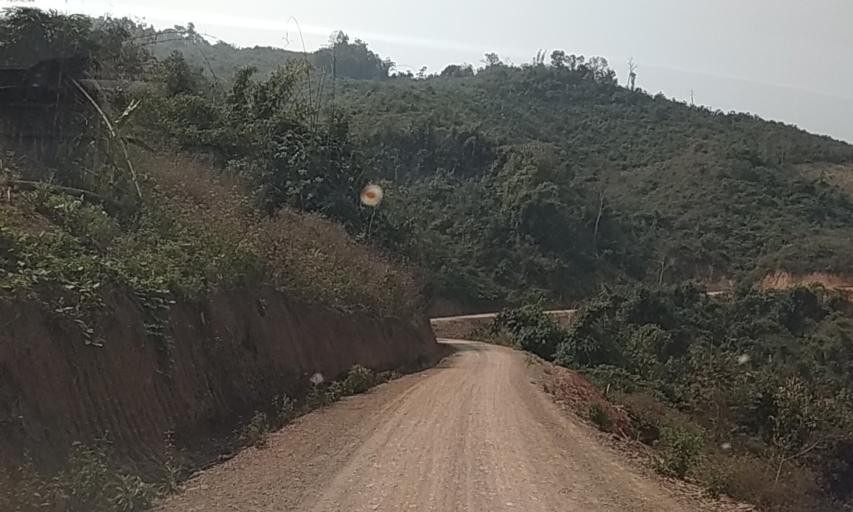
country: LA
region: Phongsali
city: Phongsali
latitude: 21.4771
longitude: 102.4403
